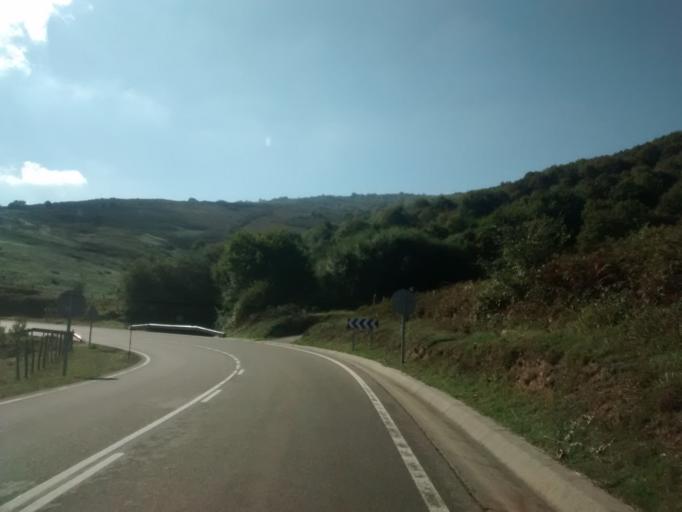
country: ES
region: Cantabria
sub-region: Provincia de Cantabria
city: Reinosa
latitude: 42.9714
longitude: -4.0783
